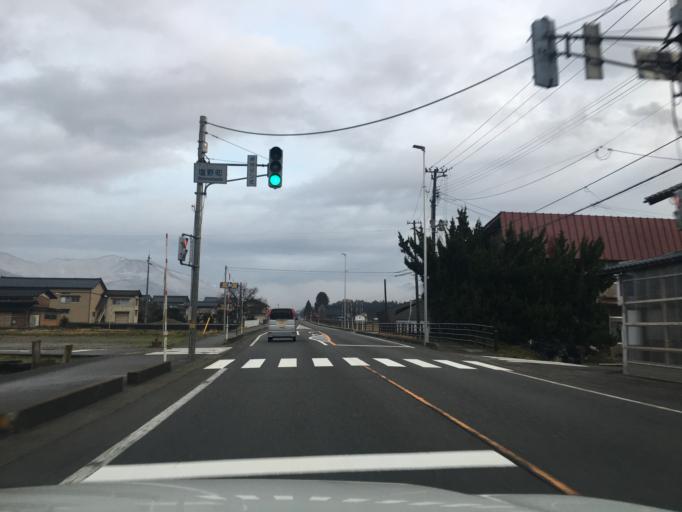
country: JP
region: Niigata
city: Murakami
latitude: 38.3259
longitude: 139.5556
